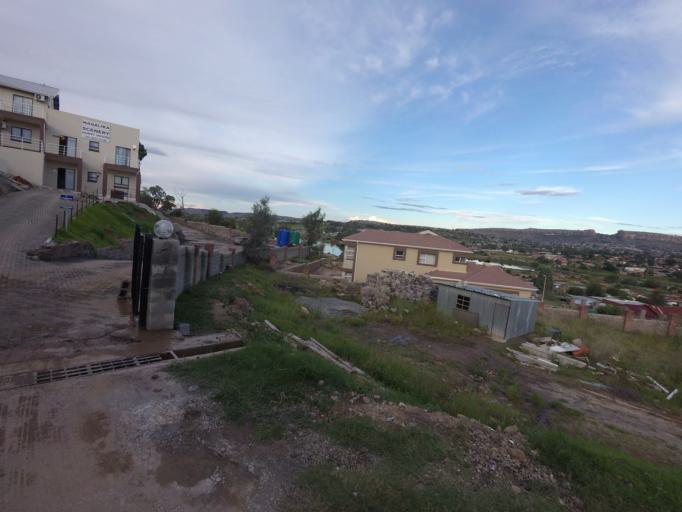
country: LS
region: Maseru
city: Maseru
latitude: -29.3053
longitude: 27.5071
